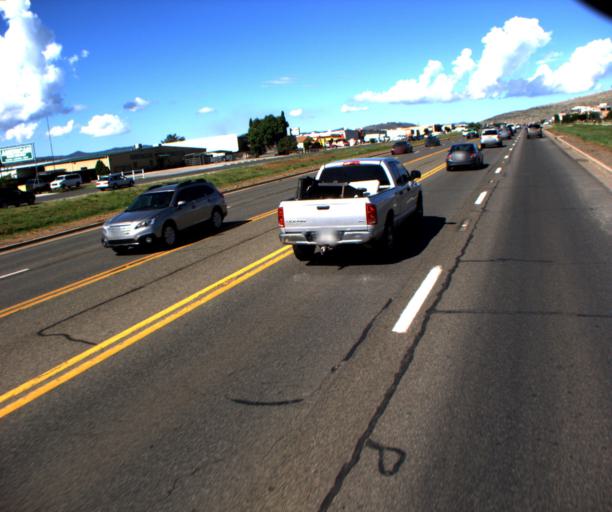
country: US
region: Arizona
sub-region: Yavapai County
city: Prescott Valley
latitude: 34.5844
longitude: -112.3361
